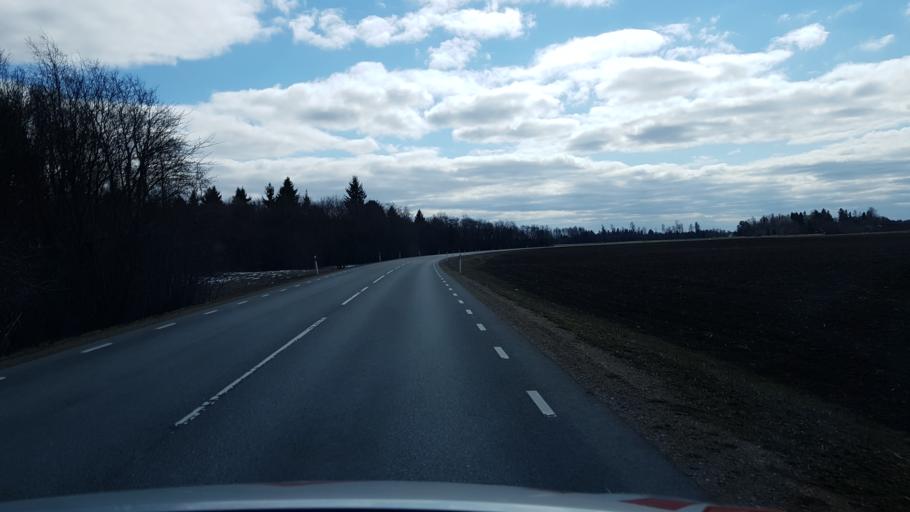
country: EE
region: Laeaene-Virumaa
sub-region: Tapa vald
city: Tapa
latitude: 59.3485
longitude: 26.0048
